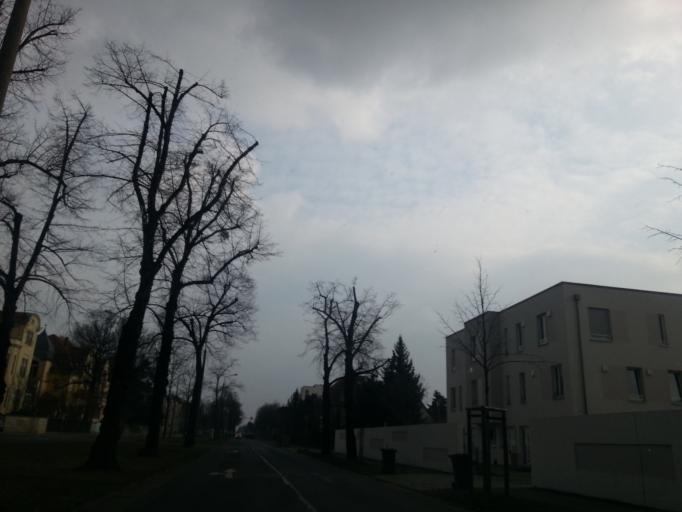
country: DE
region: Saxony
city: Dresden
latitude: 51.0317
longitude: 13.7780
